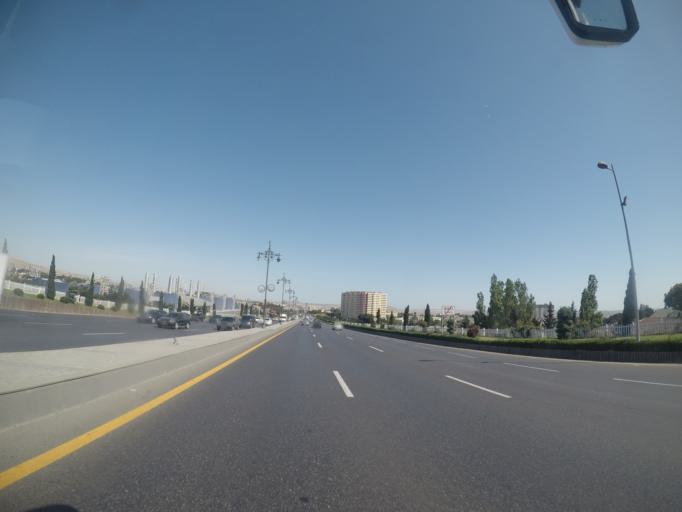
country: AZ
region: Baki
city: Bilajari
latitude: 40.4161
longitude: 49.8005
